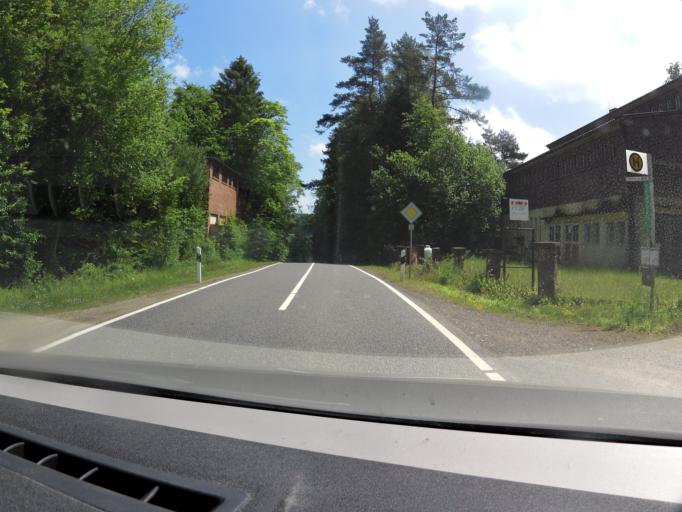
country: DE
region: Hesse
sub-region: Regierungsbezirk Kassel
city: Nentershausen
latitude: 50.9927
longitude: 9.9290
